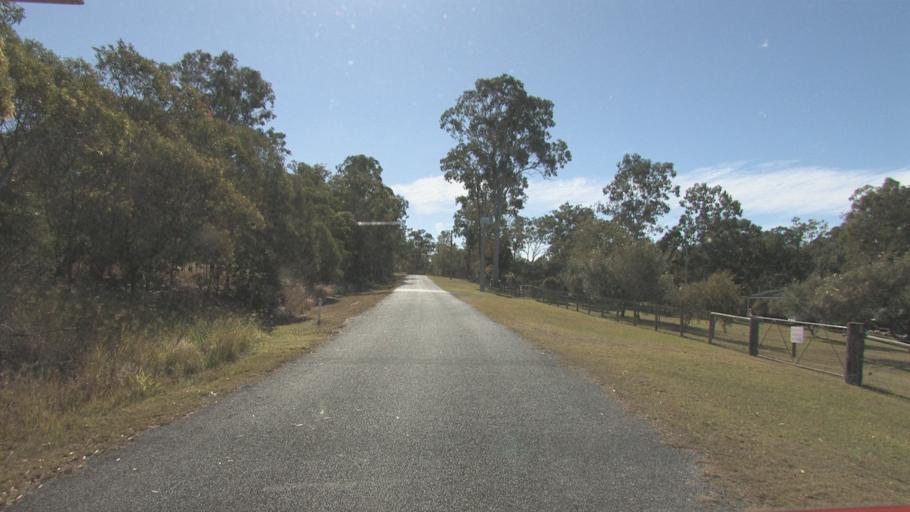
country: AU
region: Queensland
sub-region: Ipswich
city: Springfield Lakes
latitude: -27.7232
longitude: 152.9395
